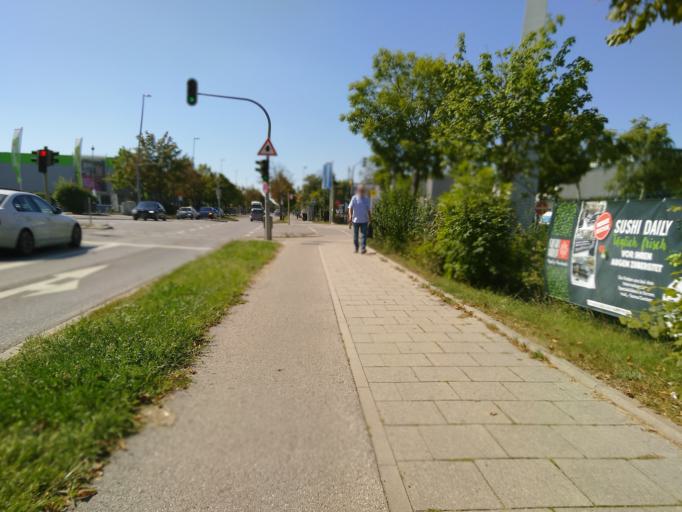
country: DE
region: Bavaria
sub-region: Upper Bavaria
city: Bogenhausen
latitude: 48.1929
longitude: 11.5970
